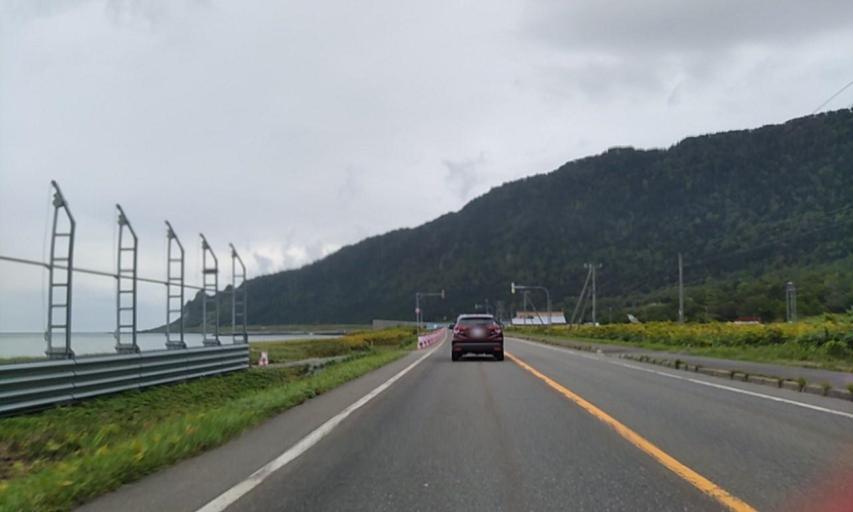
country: JP
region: Hokkaido
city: Nayoro
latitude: 45.0656
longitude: 142.4751
